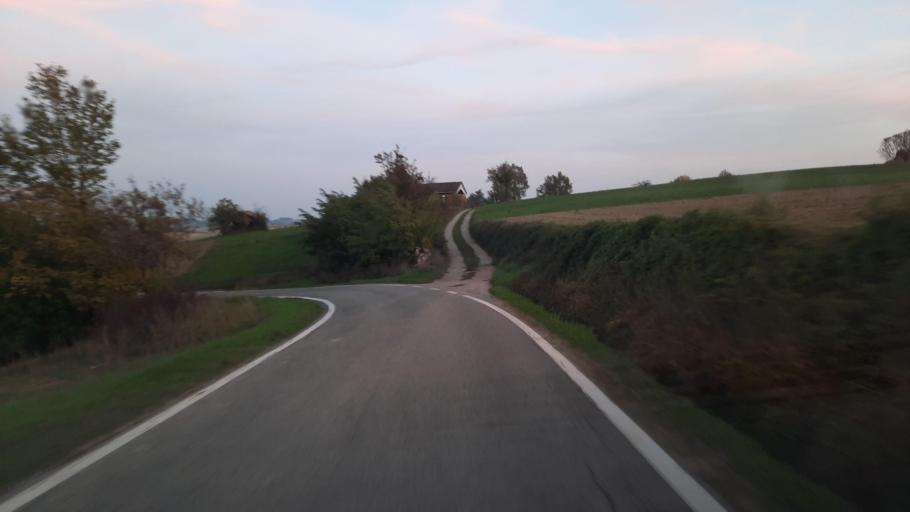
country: IT
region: Piedmont
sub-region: Provincia di Asti
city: Tonco
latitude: 45.0135
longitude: 8.2072
